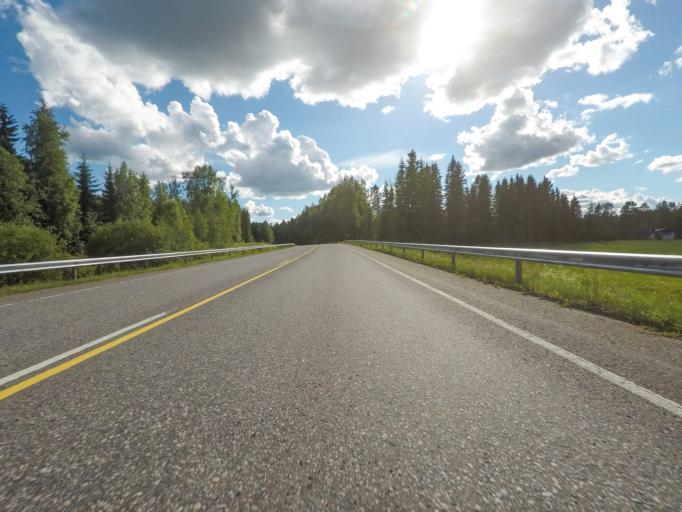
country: FI
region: Uusimaa
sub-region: Helsinki
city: Vihti
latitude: 60.4355
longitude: 24.4803
